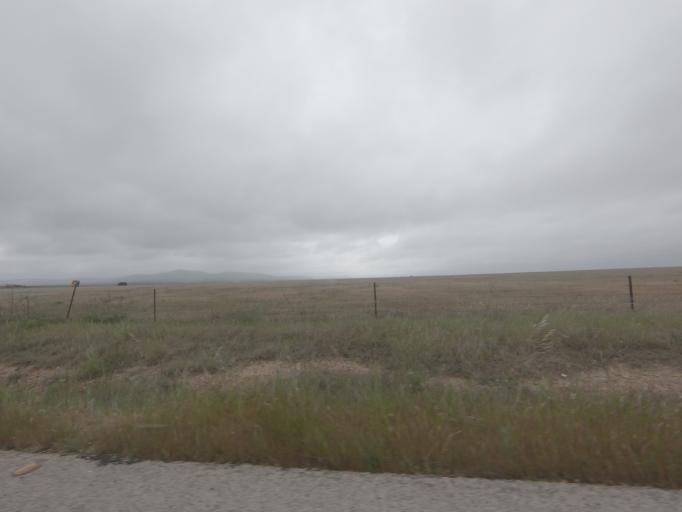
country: ES
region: Extremadura
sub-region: Provincia de Caceres
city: Malpartida de Caceres
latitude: 39.3569
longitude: -6.4657
